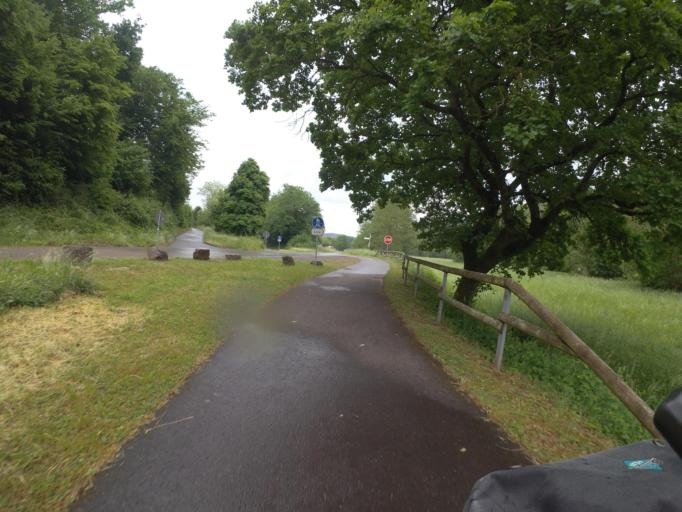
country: DE
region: Rheinland-Pfalz
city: Brauneberg
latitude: 49.9320
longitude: 6.9751
